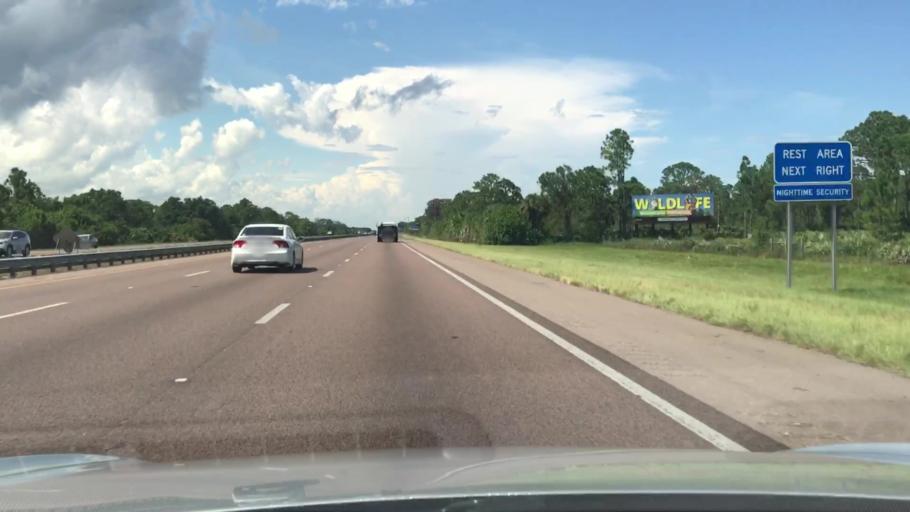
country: US
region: Florida
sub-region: Brevard County
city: Grant-Valkaria
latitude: 27.9270
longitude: -80.6026
